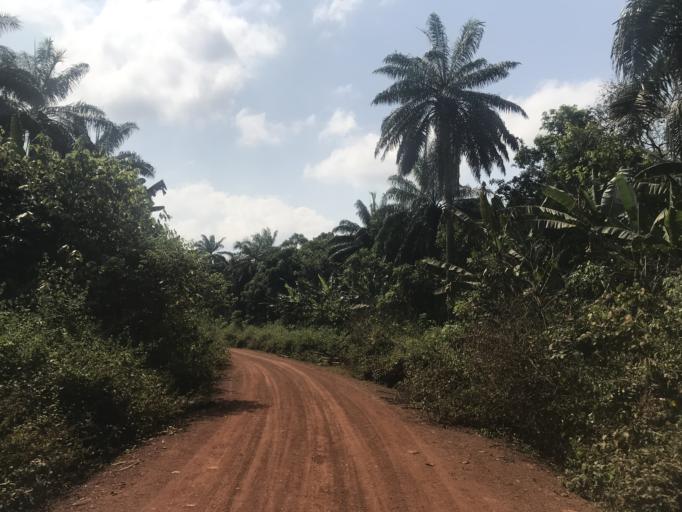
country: NG
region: Osun
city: Ibokun
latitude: 7.8111
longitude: 4.6464
